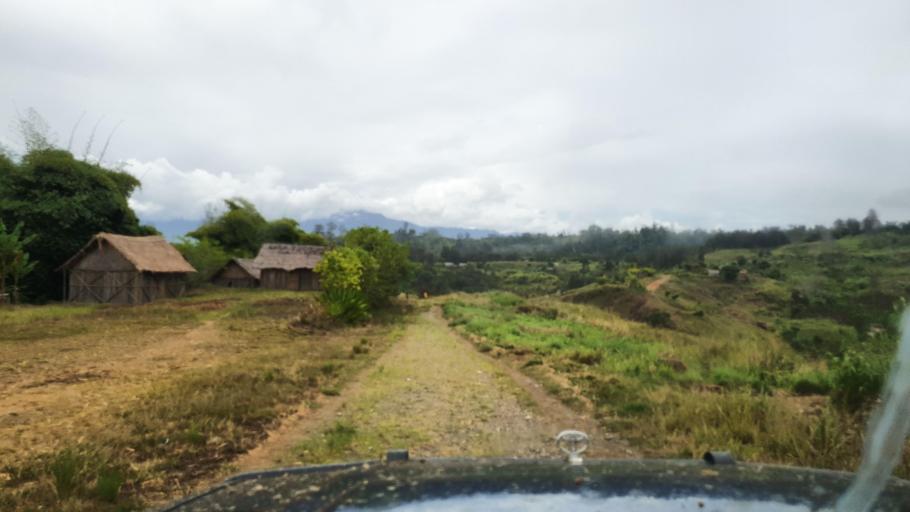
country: PG
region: Jiwaka
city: Minj
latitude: -5.9509
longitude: 144.7732
